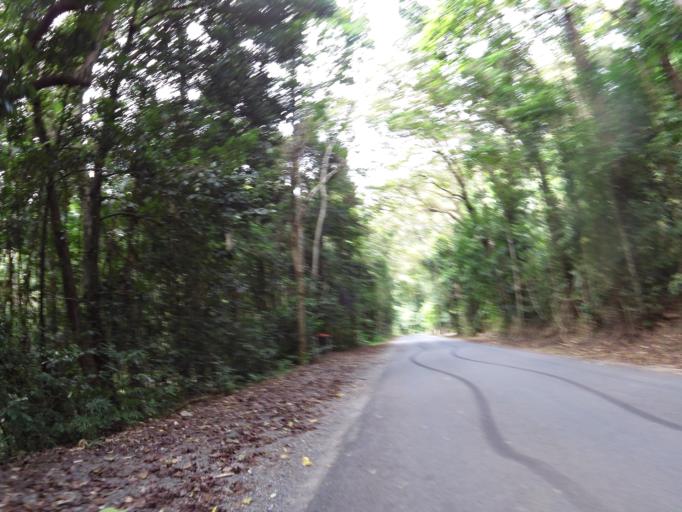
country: AU
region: Queensland
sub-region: Cairns
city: Woree
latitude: -16.9611
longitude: 145.6809
